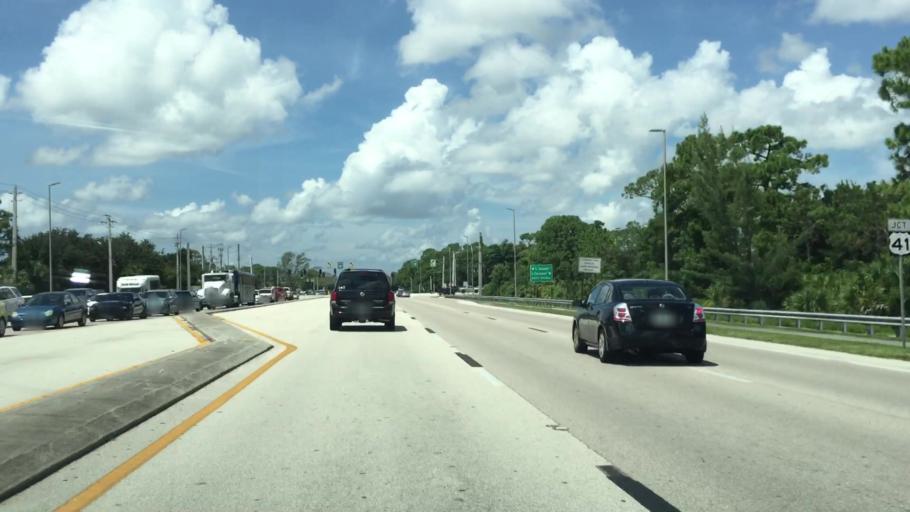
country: US
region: Florida
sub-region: Lee County
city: Villas
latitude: 26.5464
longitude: -81.8688
